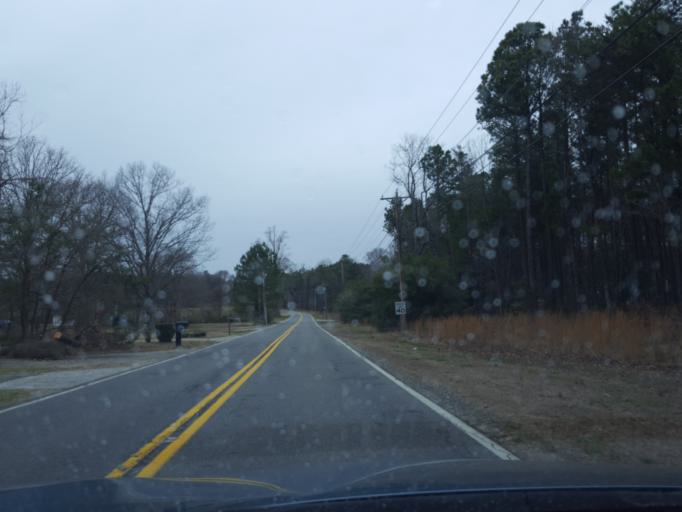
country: US
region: Maryland
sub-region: Calvert County
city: Long Beach
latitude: 38.4517
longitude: -76.5260
